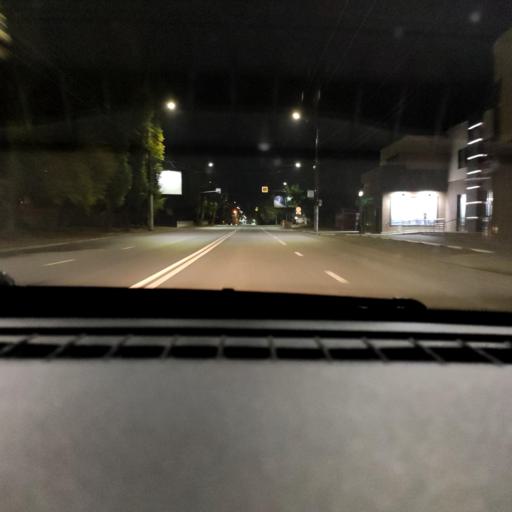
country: RU
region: Voronezj
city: Voronezh
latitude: 51.7021
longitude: 39.1674
